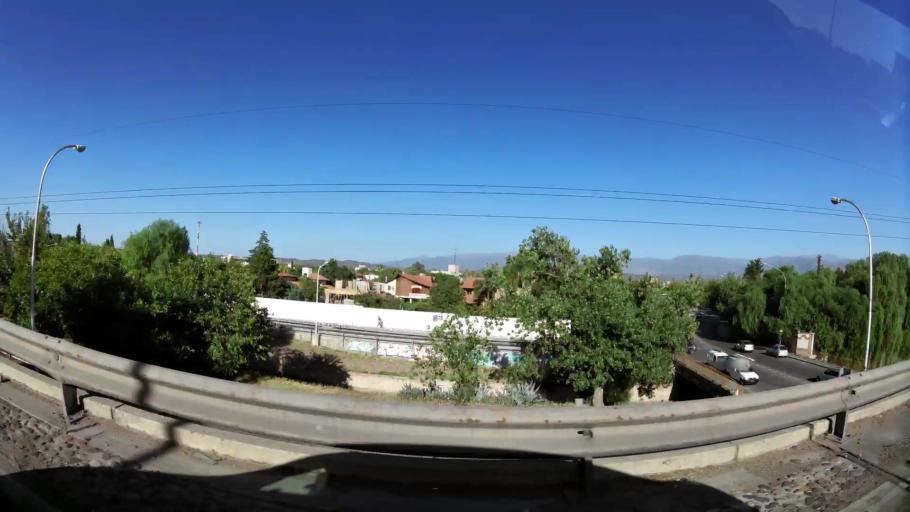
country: AR
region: Mendoza
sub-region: Departamento de Godoy Cruz
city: Godoy Cruz
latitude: -32.9131
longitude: -68.8379
